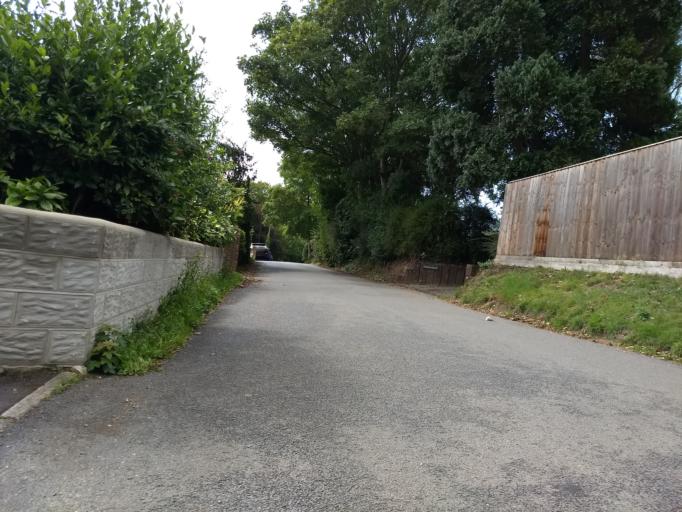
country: GB
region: England
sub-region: Isle of Wight
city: Newport
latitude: 50.6889
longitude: -1.2944
